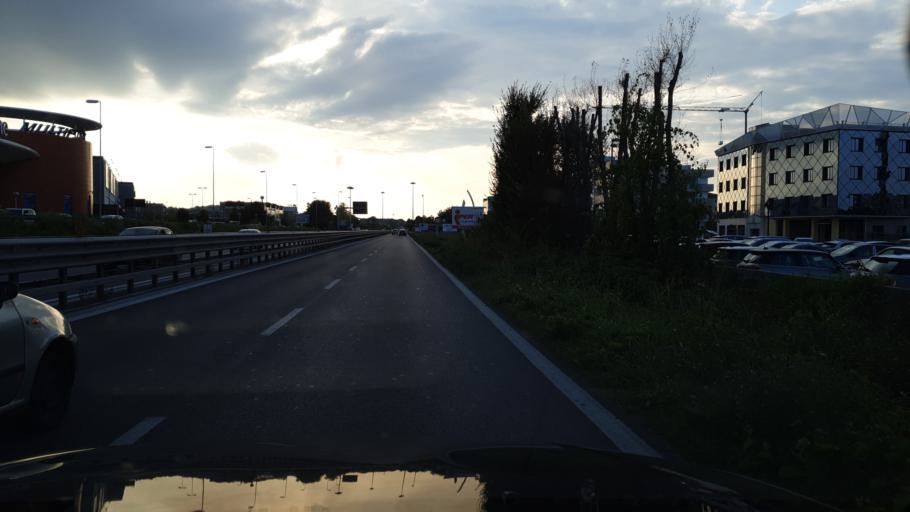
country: IT
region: Emilia-Romagna
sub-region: Provincia di Rimini
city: Rivazzurra
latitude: 44.0413
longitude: 12.5878
